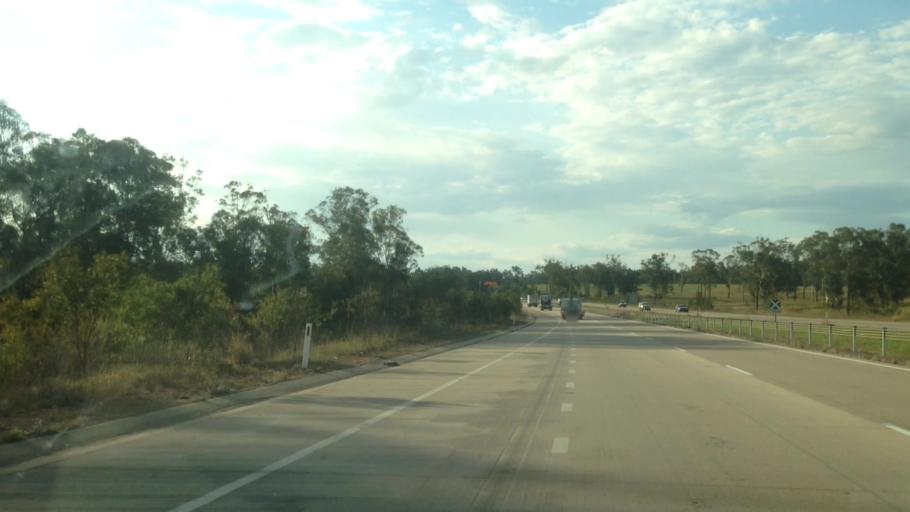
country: AU
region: New South Wales
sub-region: Cessnock
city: Heddon Greta
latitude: -32.8393
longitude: 151.5408
